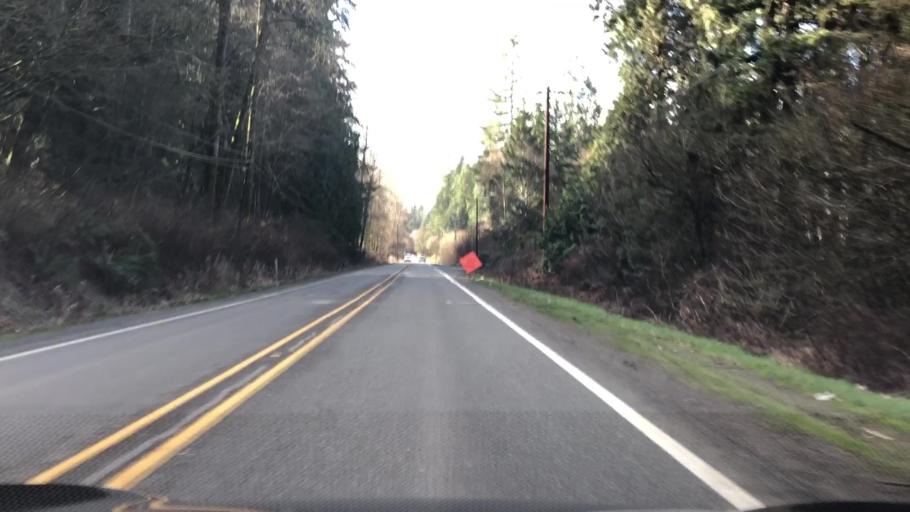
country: US
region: Washington
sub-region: Snohomish County
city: Martha Lake
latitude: 47.8260
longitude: -122.2459
